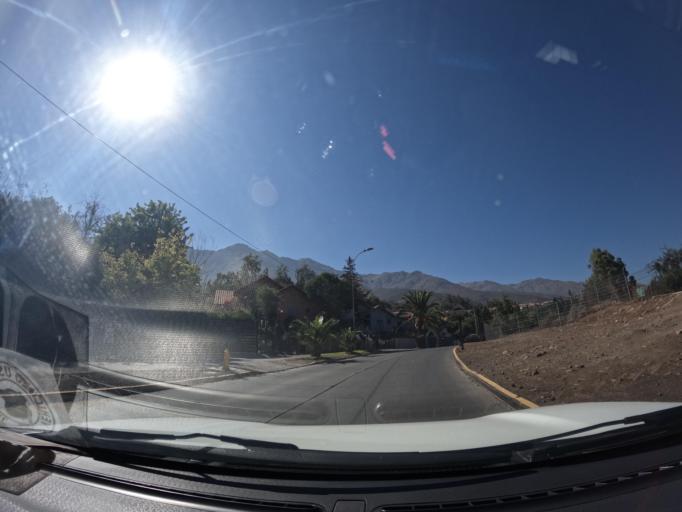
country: CL
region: Santiago Metropolitan
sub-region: Provincia de Santiago
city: Villa Presidente Frei, Nunoa, Santiago, Chile
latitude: -33.4598
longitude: -70.5208
